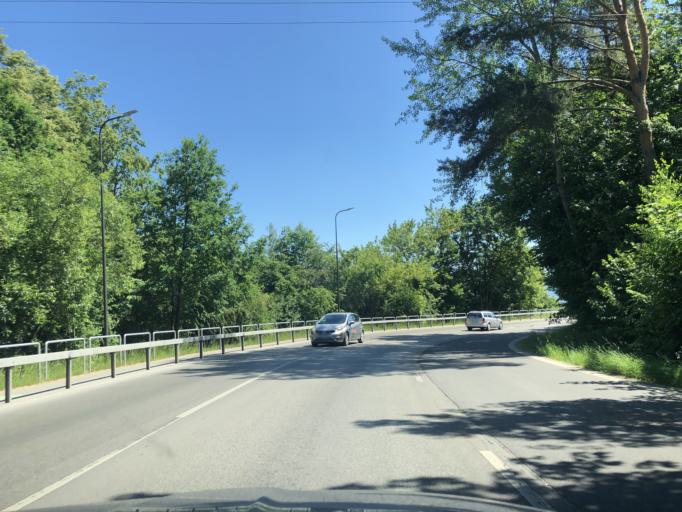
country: LT
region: Kauno apskritis
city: Dainava (Kaunas)
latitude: 54.8720
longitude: 23.9910
